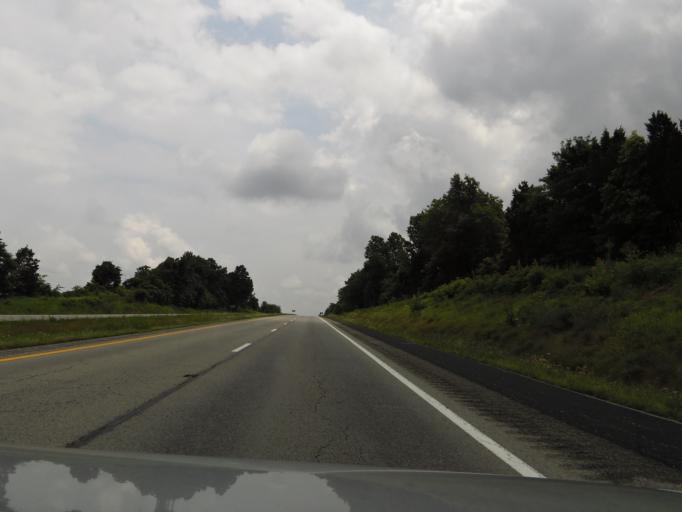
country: US
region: Kentucky
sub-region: Grayson County
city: Leitchfield
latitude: 37.5512
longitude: -86.1058
